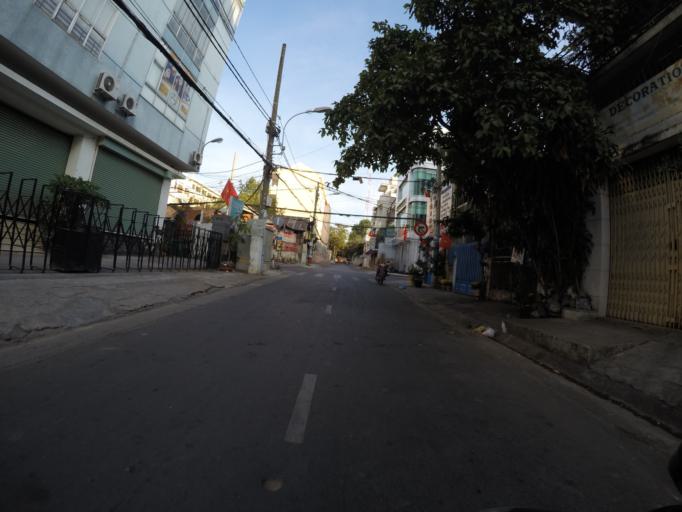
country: VN
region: Ho Chi Minh City
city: Quan Mot
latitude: 10.7908
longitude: 106.6996
